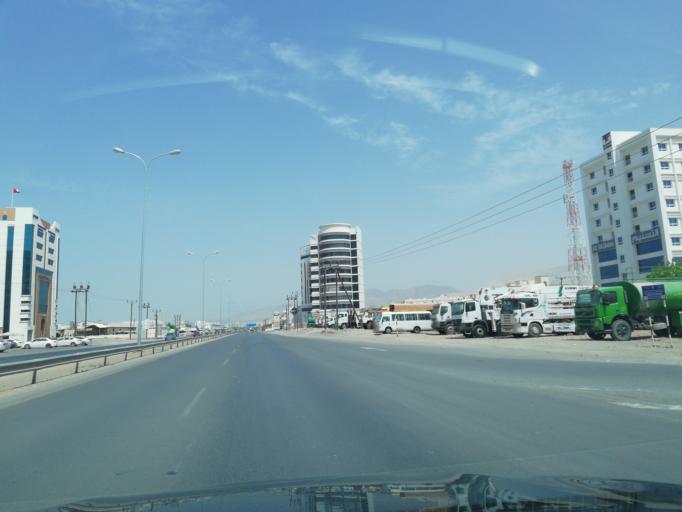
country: OM
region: Muhafazat Masqat
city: Bawshar
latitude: 23.5826
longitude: 58.3715
